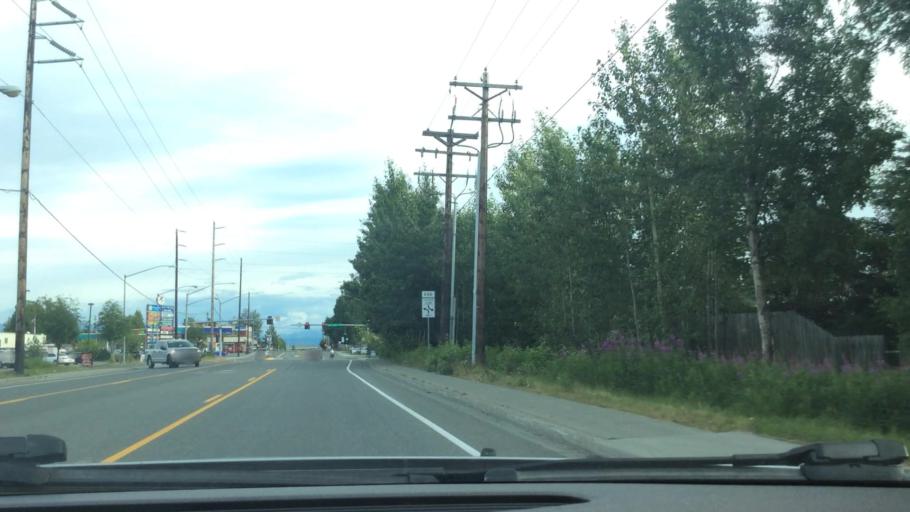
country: US
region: Alaska
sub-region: Anchorage Municipality
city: Anchorage
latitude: 61.1752
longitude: -149.8980
